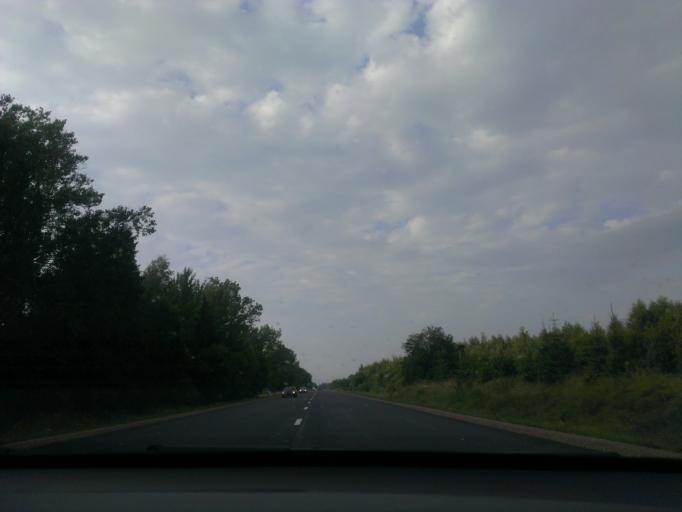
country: LV
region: Lecava
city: Iecava
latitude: 56.6730
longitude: 24.2358
